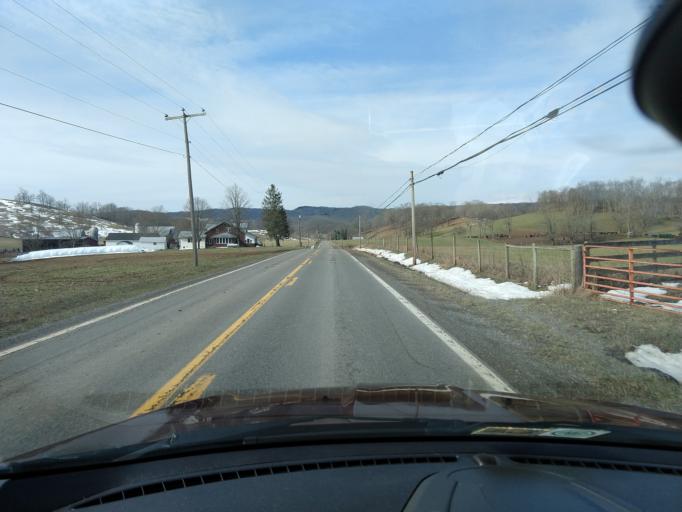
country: US
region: West Virginia
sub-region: Pocahontas County
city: Marlinton
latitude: 38.1313
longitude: -80.2199
